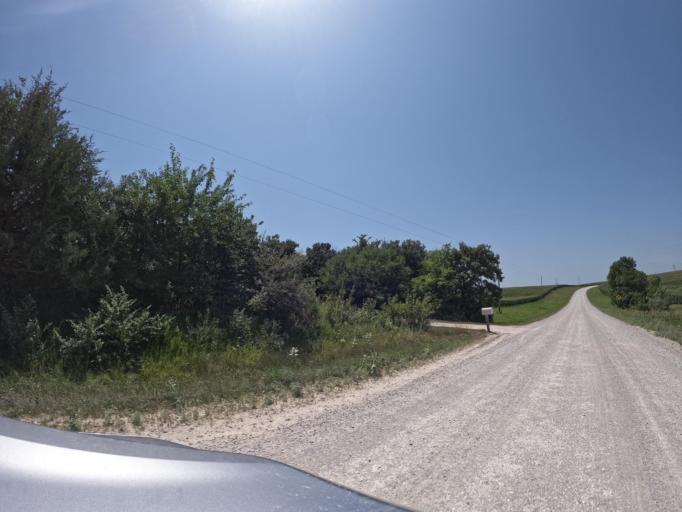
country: US
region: Iowa
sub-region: Henry County
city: Mount Pleasant
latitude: 40.9379
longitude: -91.6313
